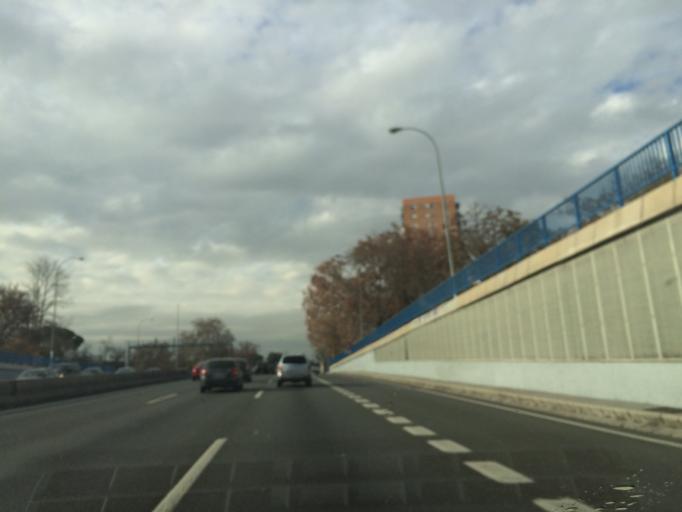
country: ES
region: Madrid
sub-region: Provincia de Madrid
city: Moncloa-Aravaca
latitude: 40.4227
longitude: -3.7263
